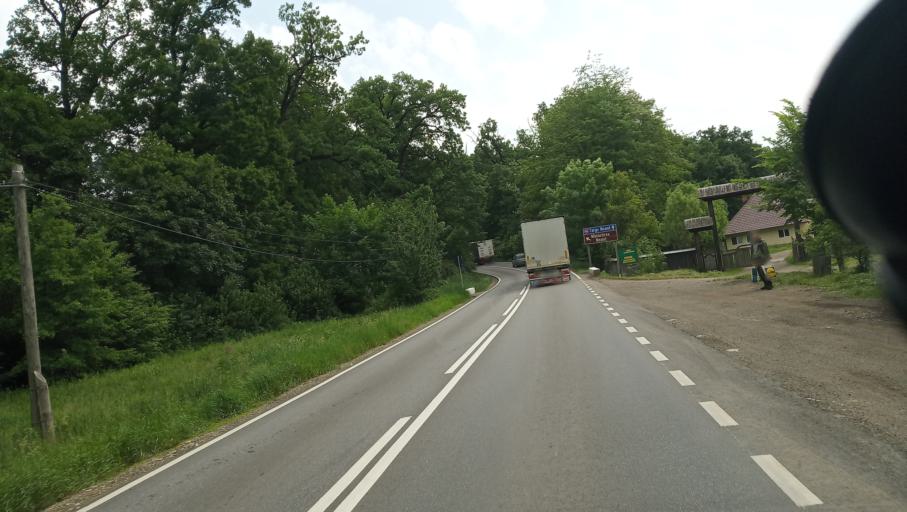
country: RO
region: Neamt
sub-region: Comuna Vanatori Neamt
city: Nemtisor
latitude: 47.2352
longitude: 26.2309
